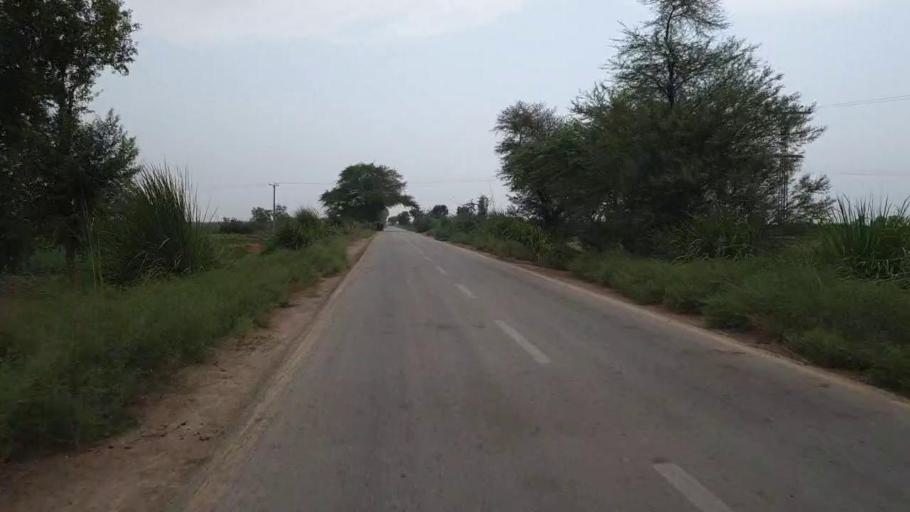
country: PK
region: Sindh
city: Bandhi
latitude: 26.5888
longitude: 68.2190
